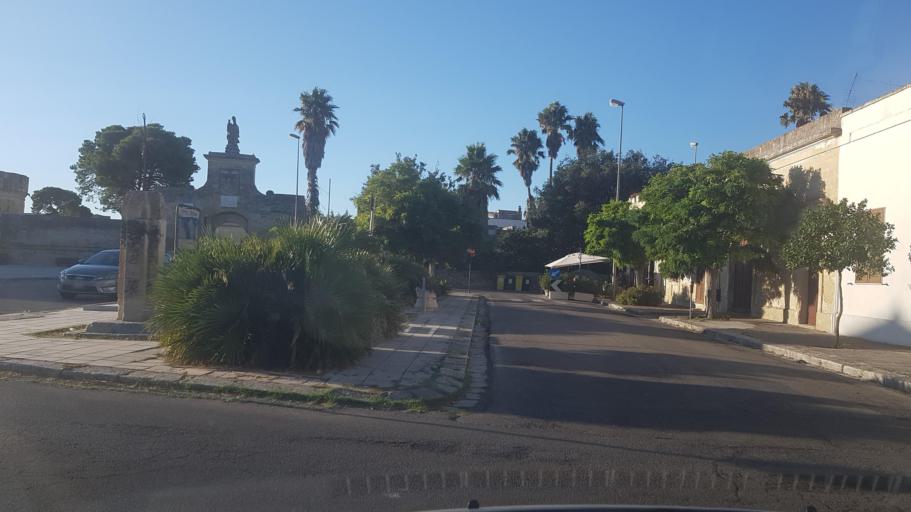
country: IT
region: Apulia
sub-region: Provincia di Lecce
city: Struda
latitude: 40.3331
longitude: 18.2970
